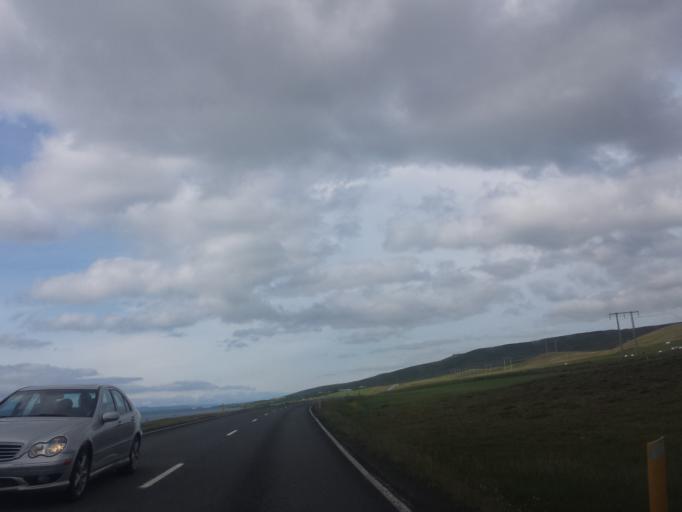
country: IS
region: West
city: Borgarnes
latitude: 65.1824
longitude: -21.0596
